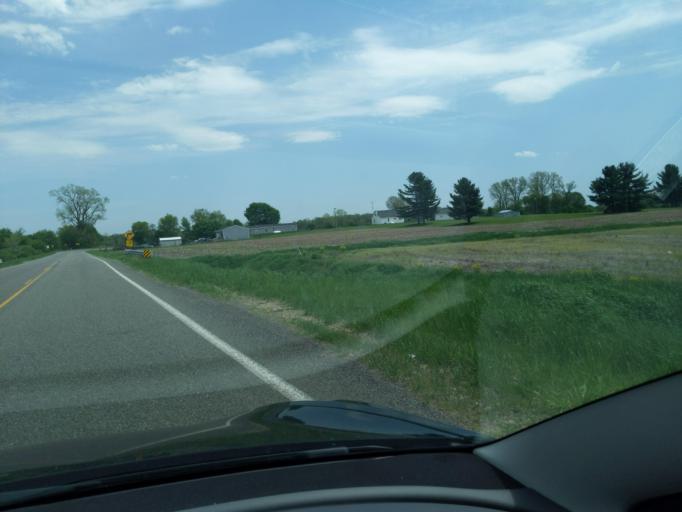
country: US
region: Michigan
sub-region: Ingham County
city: Stockbridge
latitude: 42.4899
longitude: -84.2808
